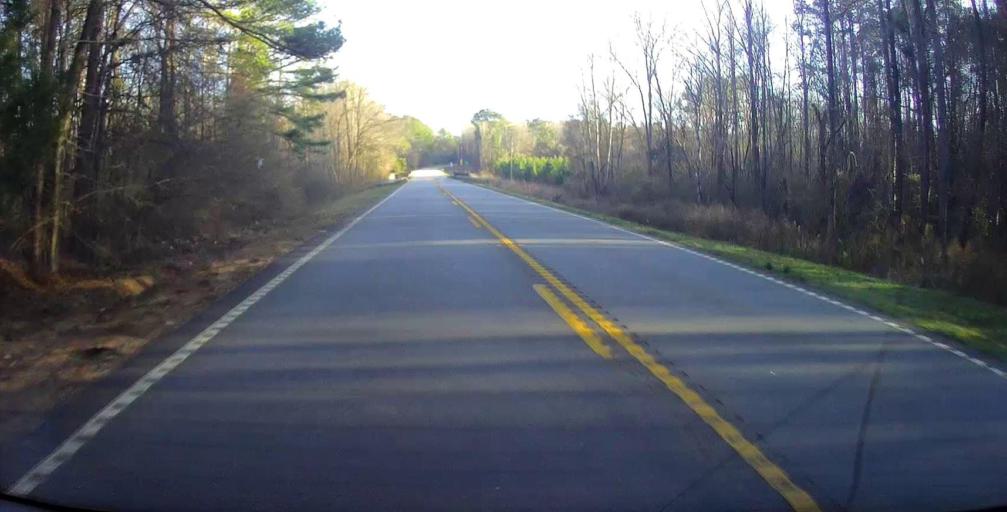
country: US
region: Alabama
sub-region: Chambers County
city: Valley
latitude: 32.8169
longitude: -85.1053
